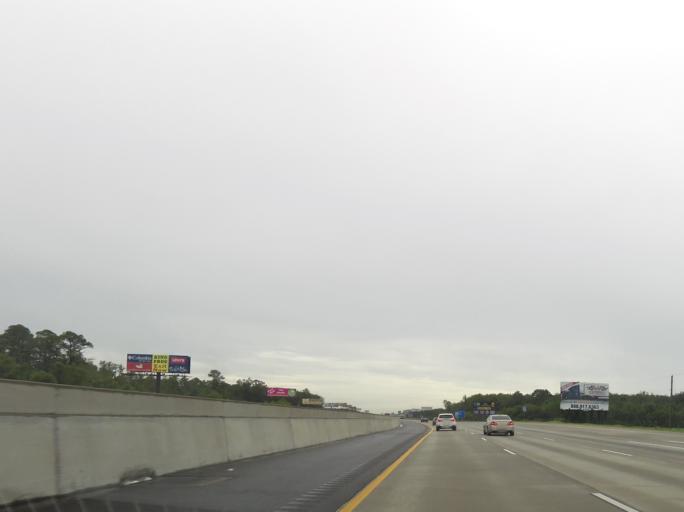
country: US
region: Georgia
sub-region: Cook County
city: Sparks
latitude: 31.1616
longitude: -83.4485
